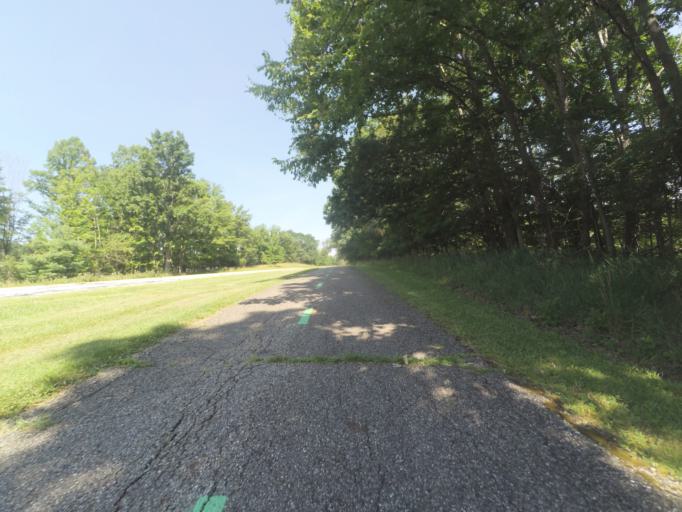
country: US
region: Ohio
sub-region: Cuyahoga County
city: Oakwood
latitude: 41.3766
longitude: -81.4936
